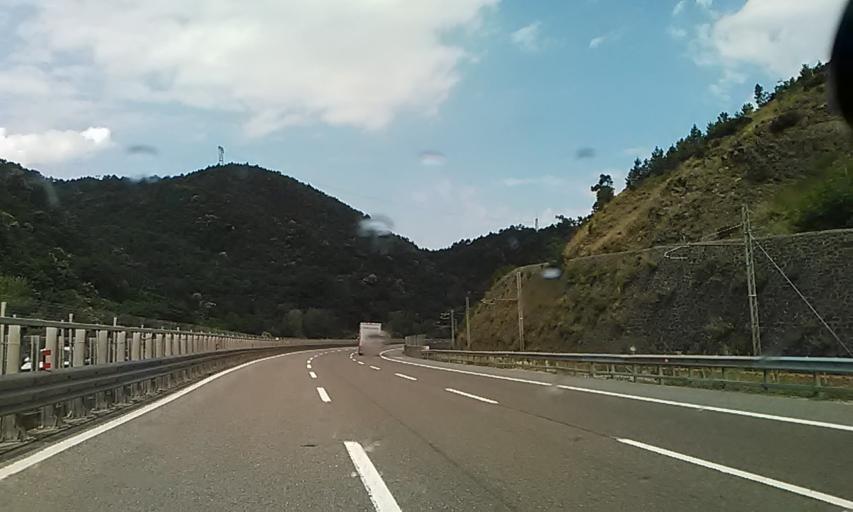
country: IT
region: Piedmont
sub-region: Provincia di Alessandria
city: Belforte Monferrato
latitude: 44.6020
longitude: 8.6654
